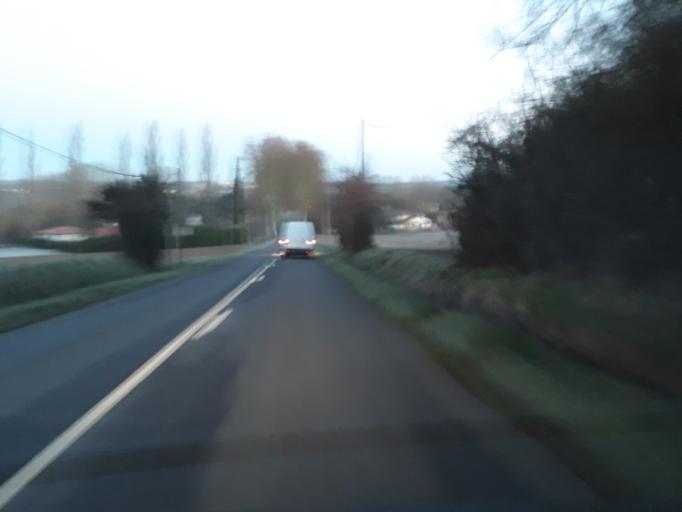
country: FR
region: Midi-Pyrenees
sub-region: Departement du Gers
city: Samatan
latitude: 43.4819
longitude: 0.9372
